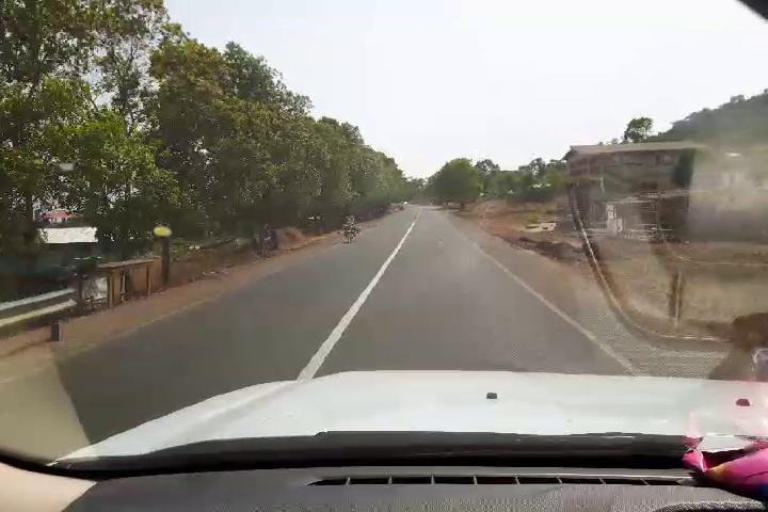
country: SL
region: Western Area
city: Waterloo
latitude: 8.2035
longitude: -13.1126
